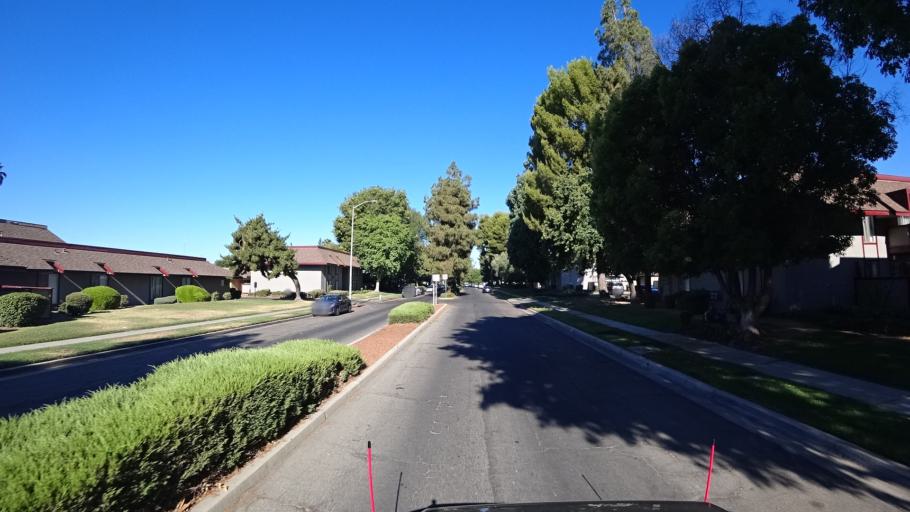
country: US
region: California
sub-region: Fresno County
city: Fresno
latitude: 36.8057
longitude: -119.8423
